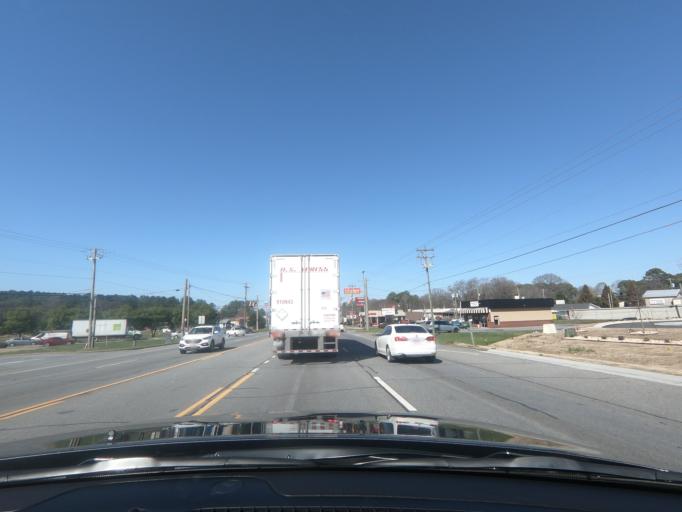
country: US
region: Georgia
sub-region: Gordon County
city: Calhoun
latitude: 34.4740
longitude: -84.9248
